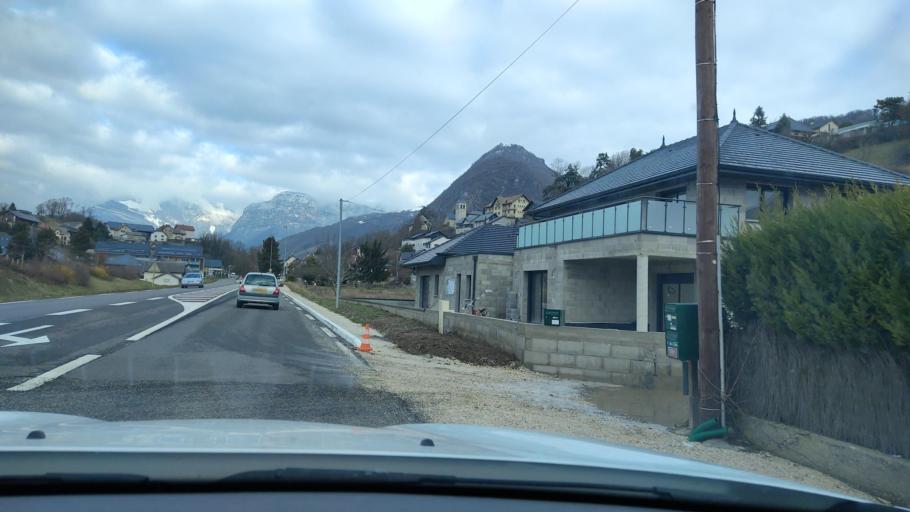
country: FR
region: Rhone-Alpes
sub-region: Departement de la Savoie
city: Challes-les-Eaux
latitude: 45.5292
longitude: 5.9927
